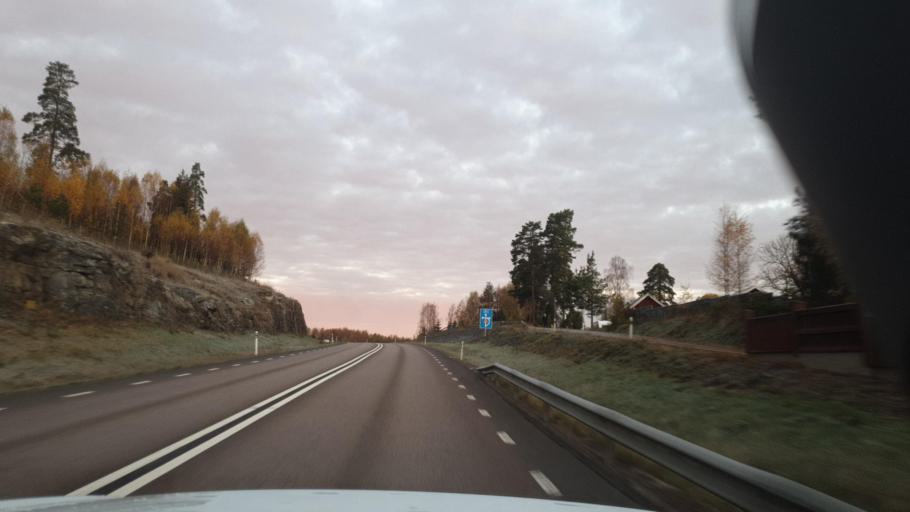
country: SE
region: Vaermland
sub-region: Eda Kommun
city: Amotfors
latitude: 59.7816
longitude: 12.3632
